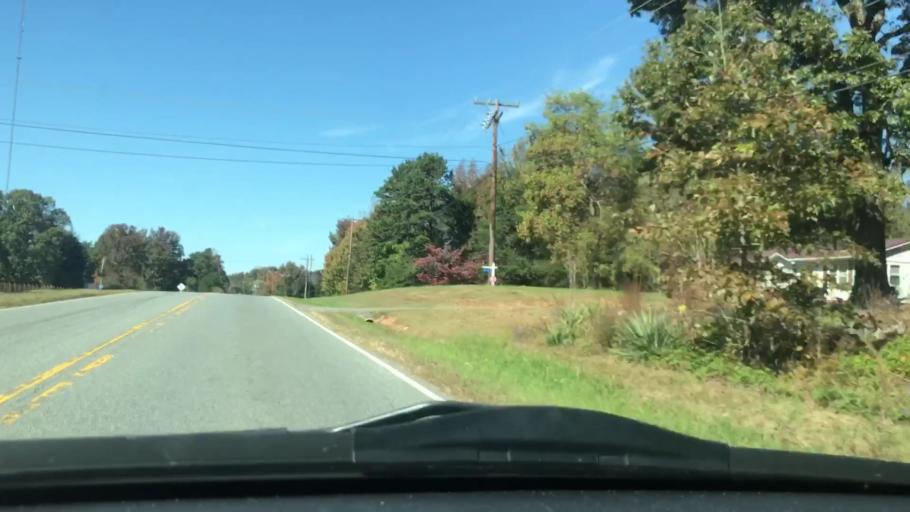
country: US
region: North Carolina
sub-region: Randolph County
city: Randleman
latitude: 35.8062
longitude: -79.8302
